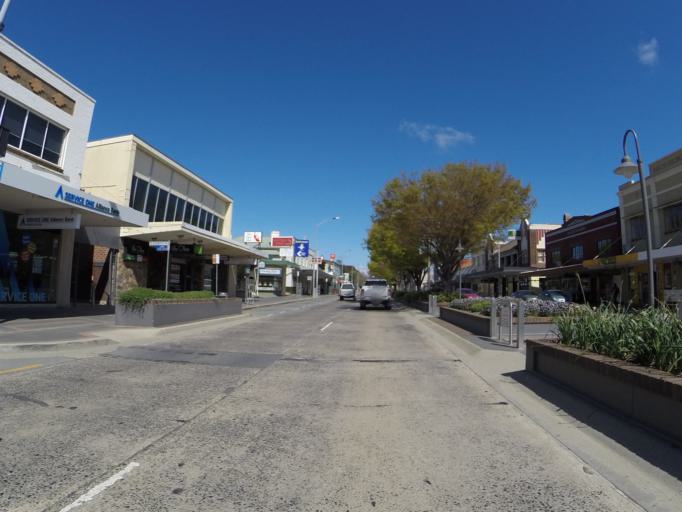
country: AU
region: New South Wales
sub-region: Queanbeyan
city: Queanbeyan
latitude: -35.3536
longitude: 149.2340
